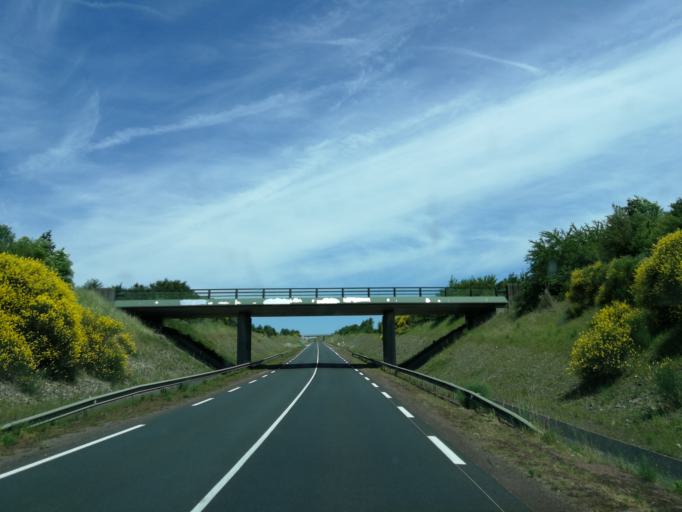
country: FR
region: Pays de la Loire
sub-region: Departement de la Vendee
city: Serigne
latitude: 46.4935
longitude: -0.8315
